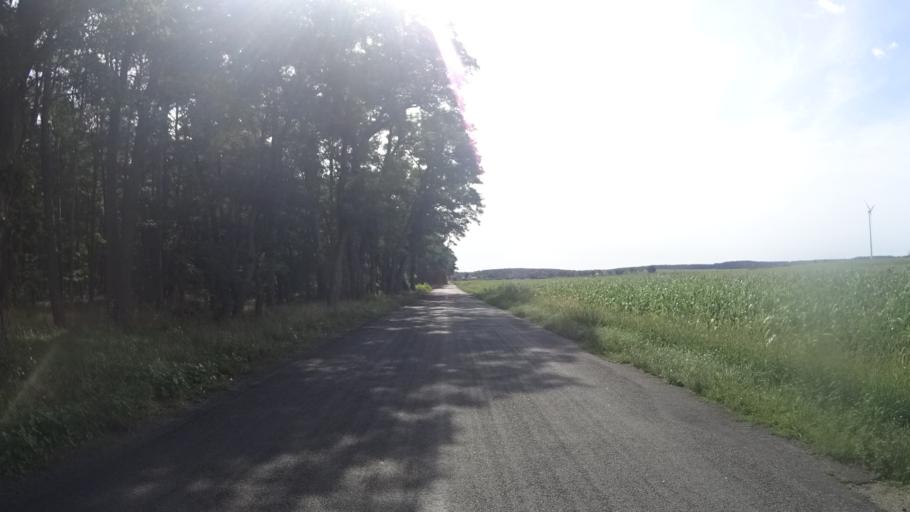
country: DE
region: Brandenburg
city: Golzow
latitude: 52.3163
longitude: 12.6872
